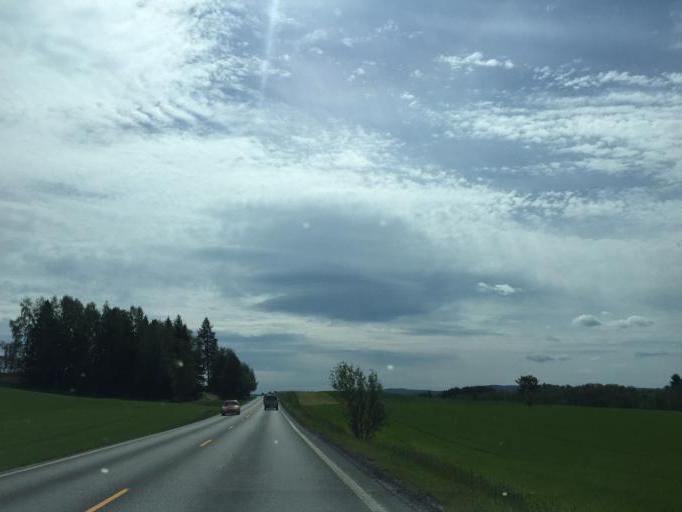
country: NO
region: Akershus
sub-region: Nes
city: Arnes
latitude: 60.1319
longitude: 11.4394
